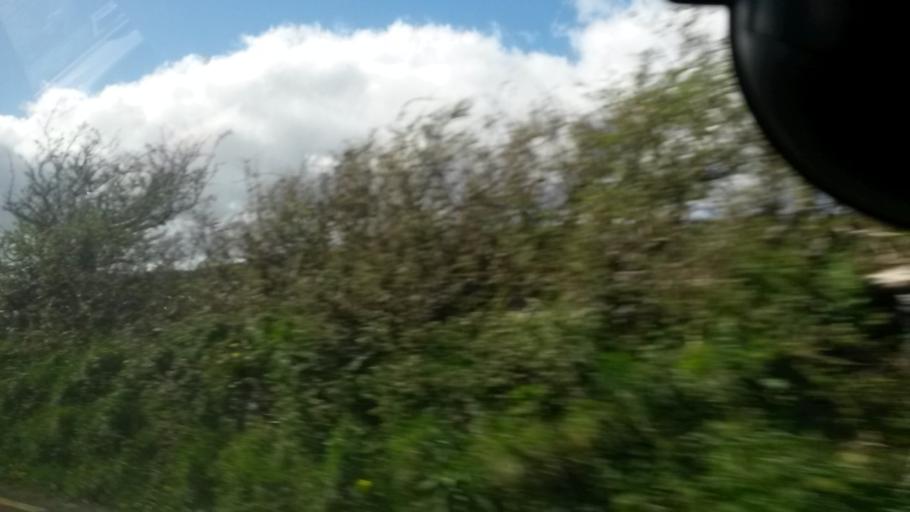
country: IE
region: Munster
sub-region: Ciarrai
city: Dingle
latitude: 52.1449
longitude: -10.2563
